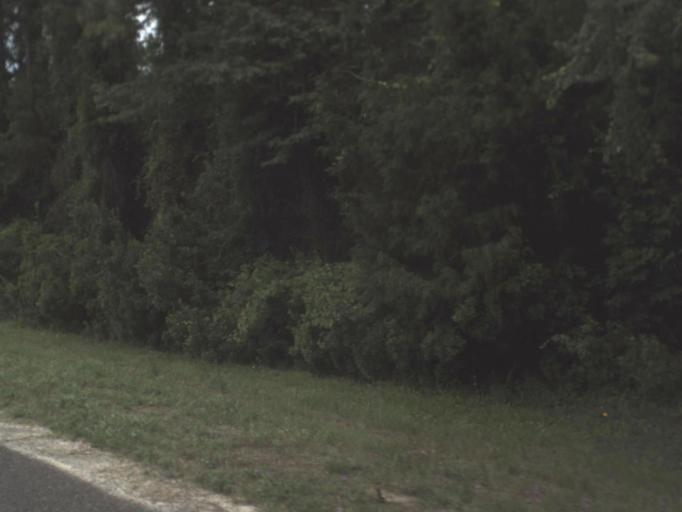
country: US
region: Florida
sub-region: Nassau County
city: Hilliard
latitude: 30.7475
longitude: -81.9573
